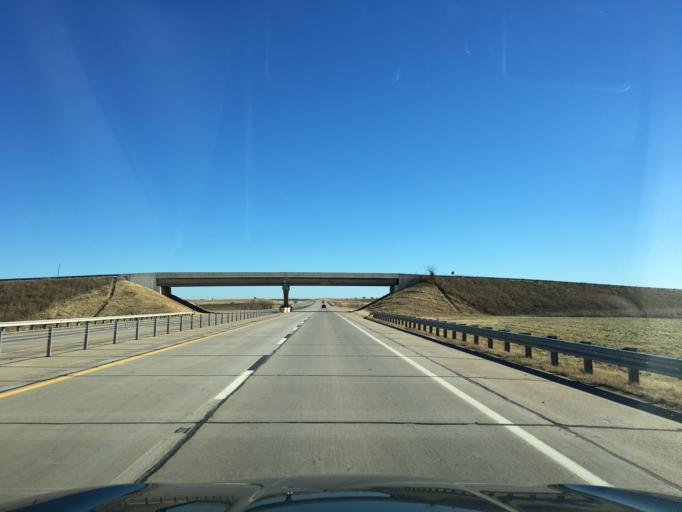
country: US
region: Oklahoma
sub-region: Noble County
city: Perry
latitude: 36.3970
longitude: -97.2307
